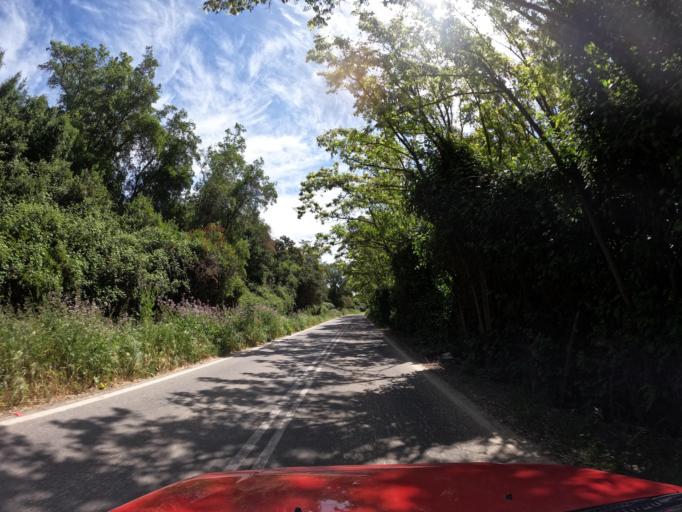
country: CL
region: Maule
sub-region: Provincia de Talca
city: Talca
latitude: -34.9892
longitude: -71.8263
